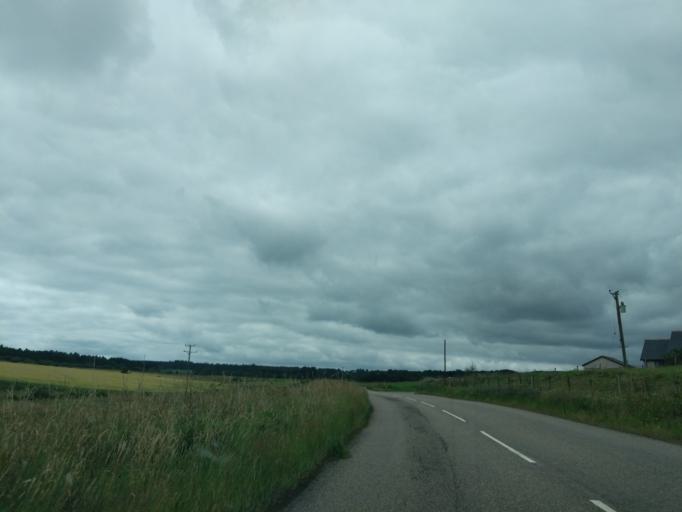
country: GB
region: Scotland
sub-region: Moray
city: Rothes
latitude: 57.4905
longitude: -3.2269
